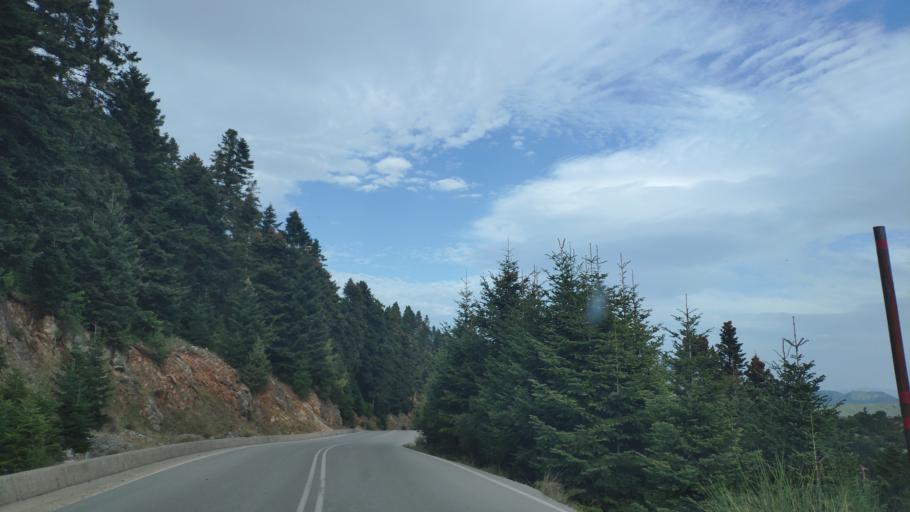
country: GR
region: Central Greece
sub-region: Nomos Fokidos
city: Amfissa
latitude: 38.6583
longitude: 22.3821
